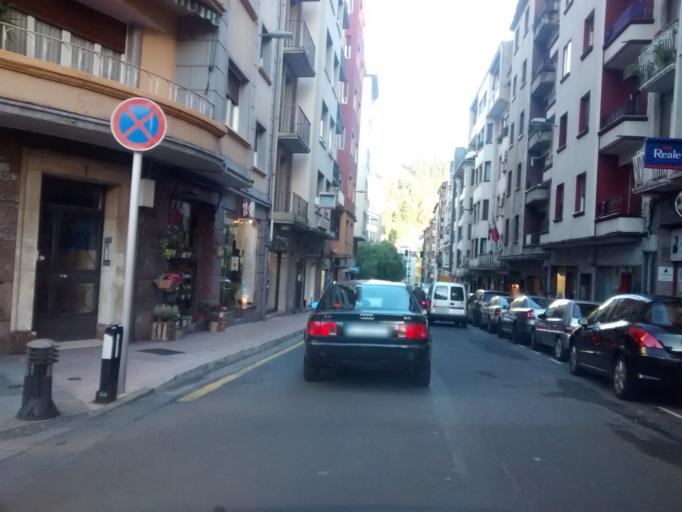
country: ES
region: Basque Country
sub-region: Provincia de Guipuzcoa
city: Eibar
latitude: 43.1852
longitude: -2.4701
